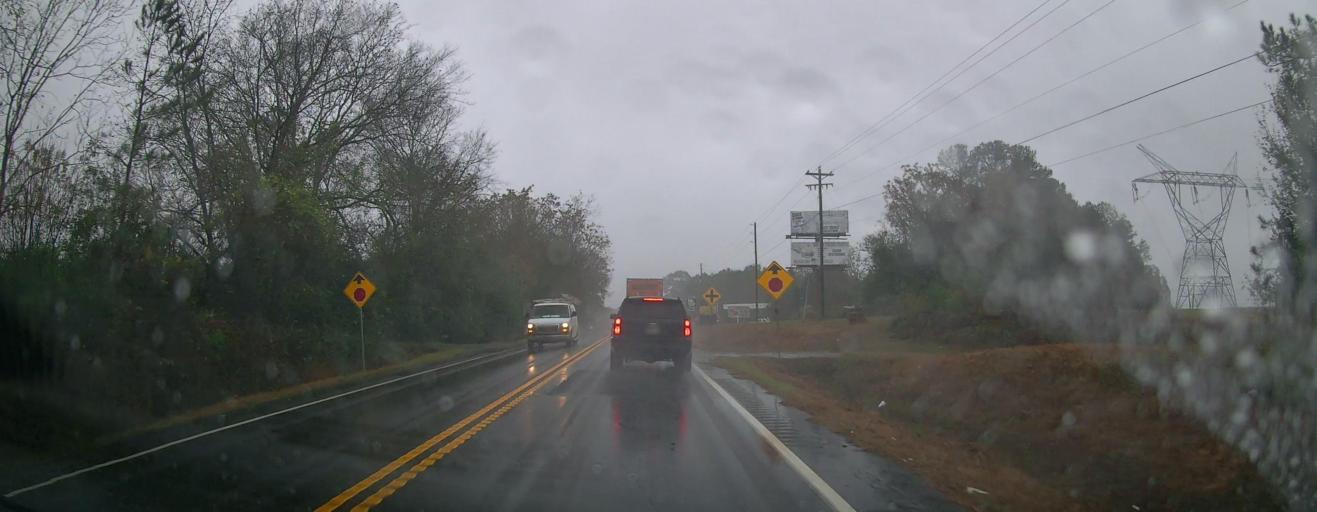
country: US
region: Georgia
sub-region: Putnam County
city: Eatonton
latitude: 33.1994
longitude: -83.4344
